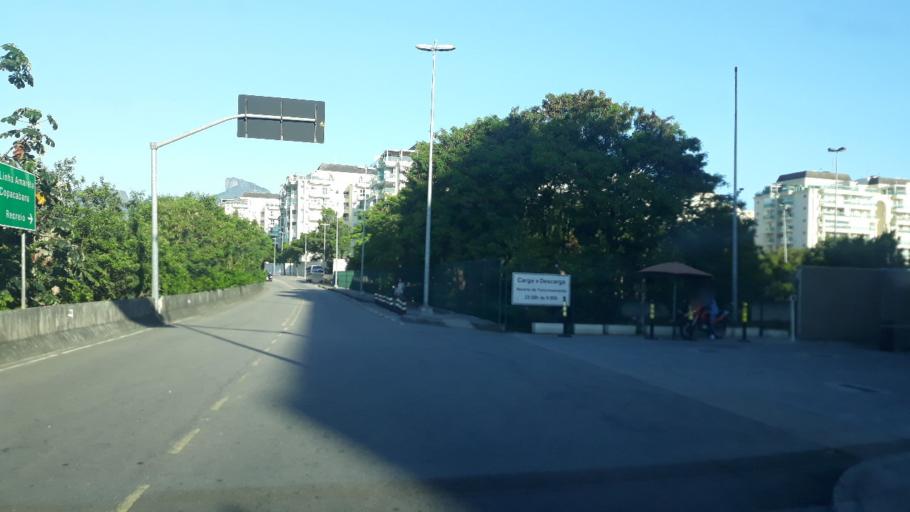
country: BR
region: Rio de Janeiro
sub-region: Rio De Janeiro
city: Rio de Janeiro
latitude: -22.9968
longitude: -43.3510
